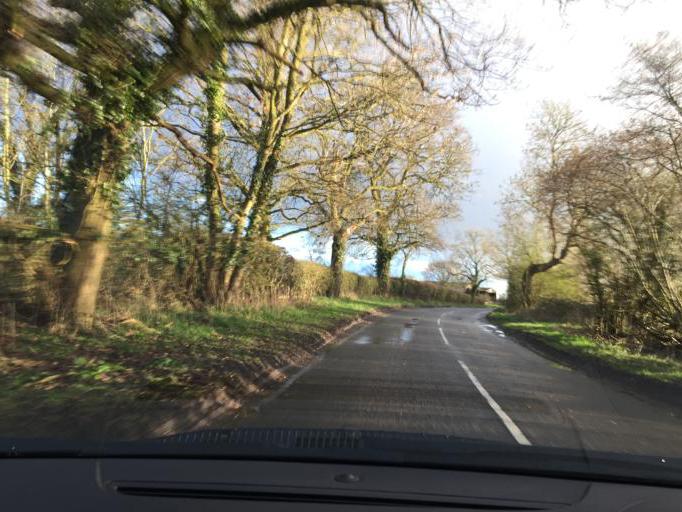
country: GB
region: England
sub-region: Warwickshire
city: Wroxall
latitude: 52.2670
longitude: -1.6928
